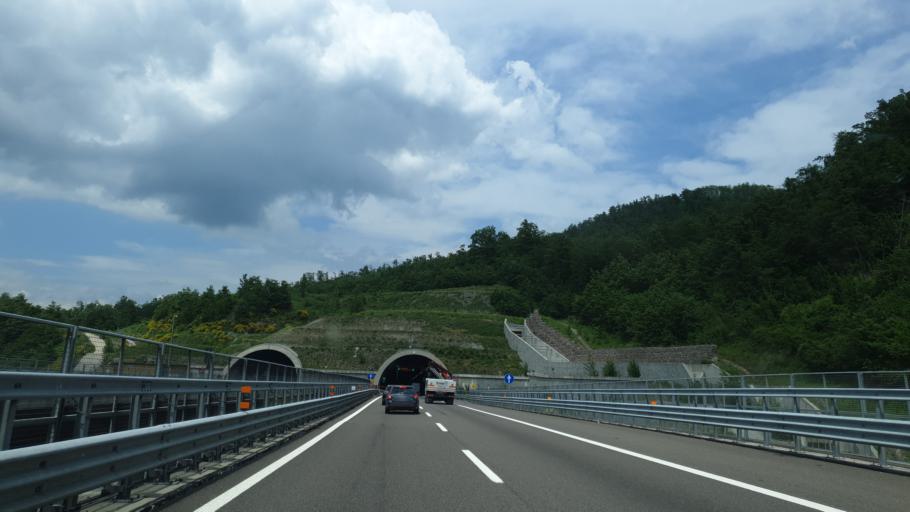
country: IT
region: Emilia-Romagna
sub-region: Provincia di Bologna
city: San Benedetto Val di Sambro
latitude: 44.1932
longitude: 11.2004
